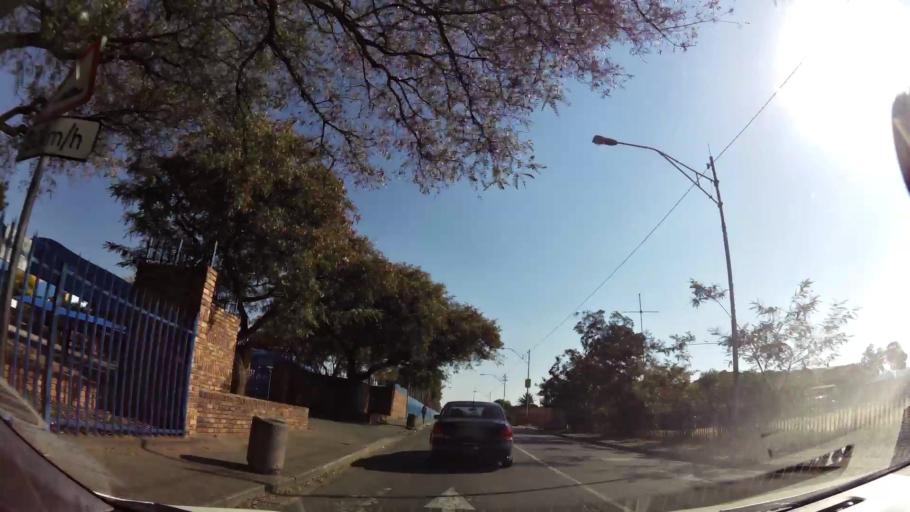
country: ZA
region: Gauteng
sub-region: City of Johannesburg Metropolitan Municipality
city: Johannesburg
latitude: -26.2586
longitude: 28.0524
